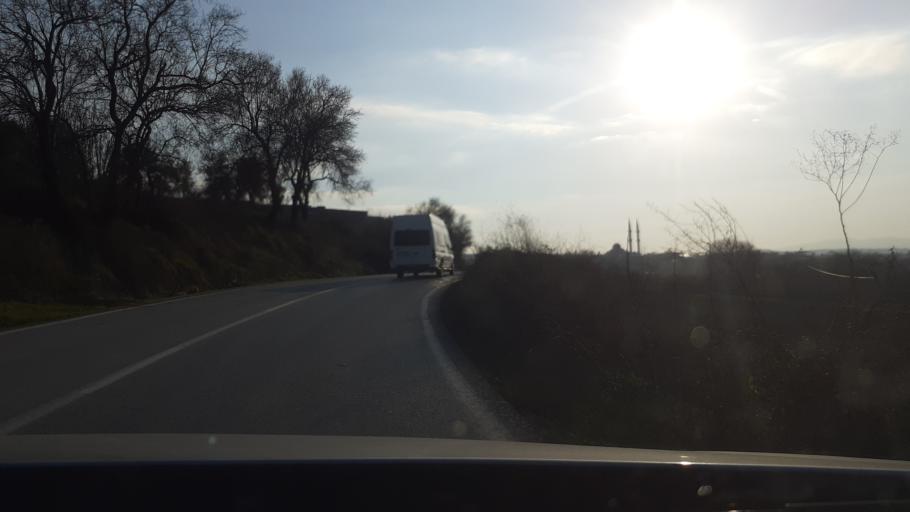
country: TR
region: Hatay
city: Oymakli
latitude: 36.1160
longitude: 36.3032
